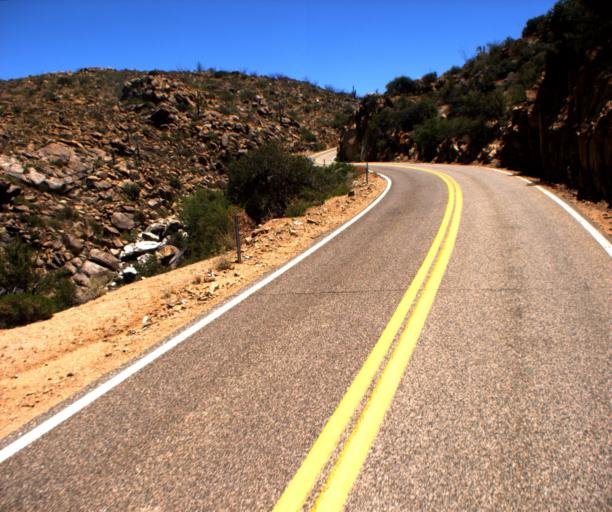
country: US
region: Arizona
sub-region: Yavapai County
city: Bagdad
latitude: 34.4500
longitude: -112.9747
